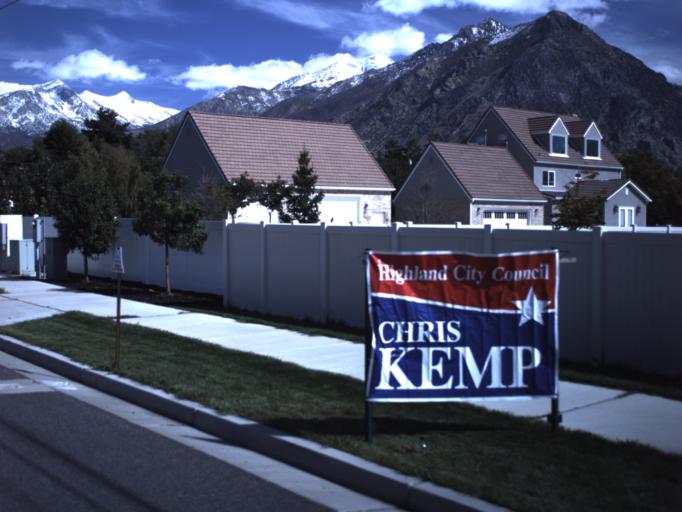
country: US
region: Utah
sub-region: Utah County
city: Cedar Hills
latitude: 40.4211
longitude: -111.7734
